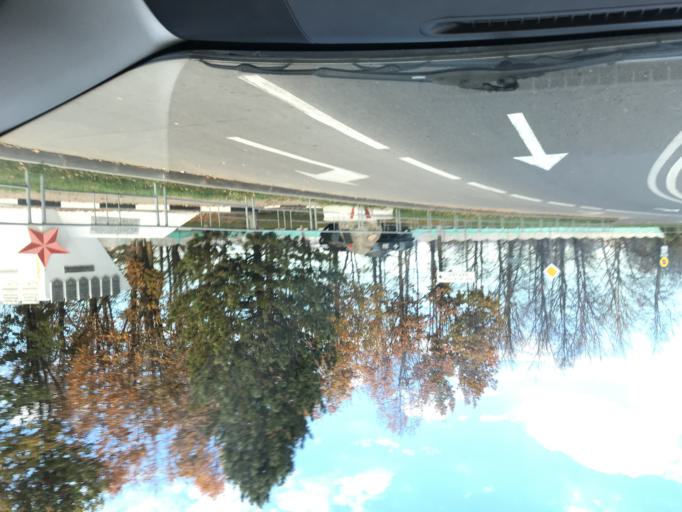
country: BY
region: Vitebsk
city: Haradok
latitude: 55.4619
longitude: 29.9873
